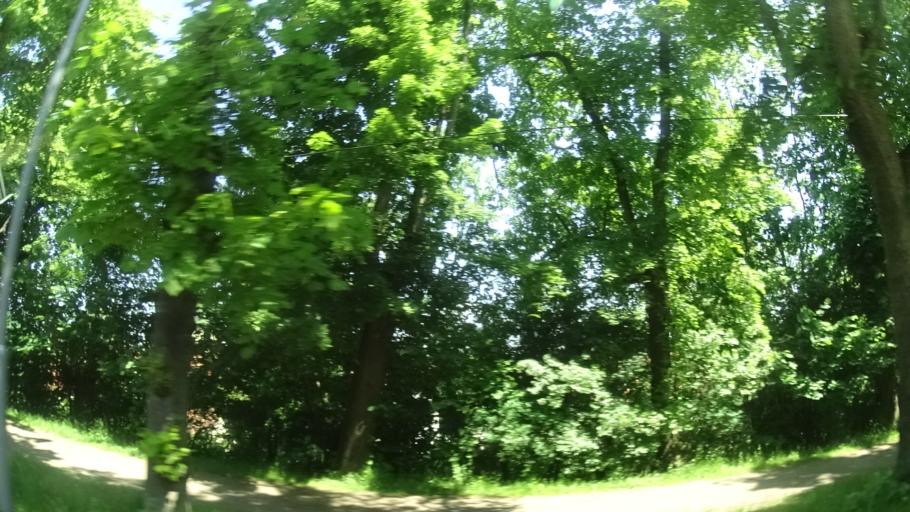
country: DE
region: Thuringia
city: Arnstadt
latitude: 50.8302
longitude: 10.9467
